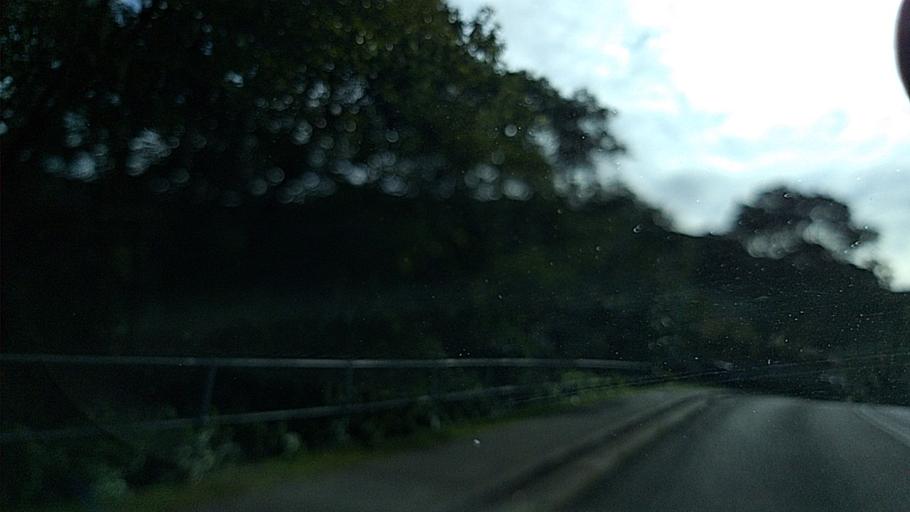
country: AU
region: New South Wales
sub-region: Wollongong
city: Bulli
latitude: -34.3082
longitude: 150.9290
